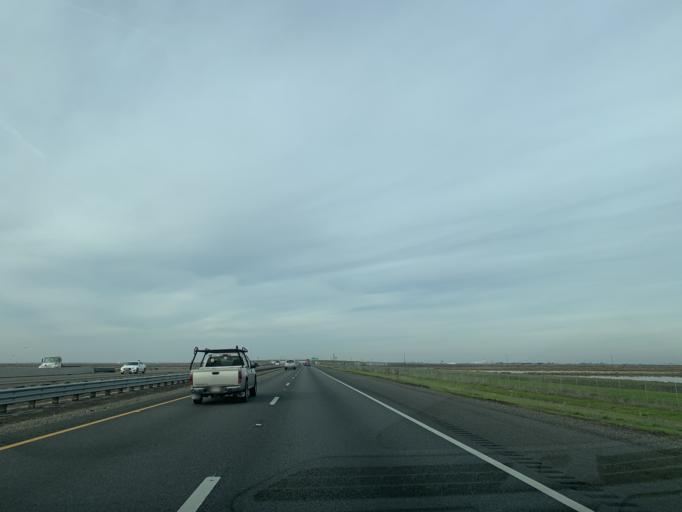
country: US
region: California
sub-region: Sacramento County
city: Elverta
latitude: 38.7390
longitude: -121.5402
